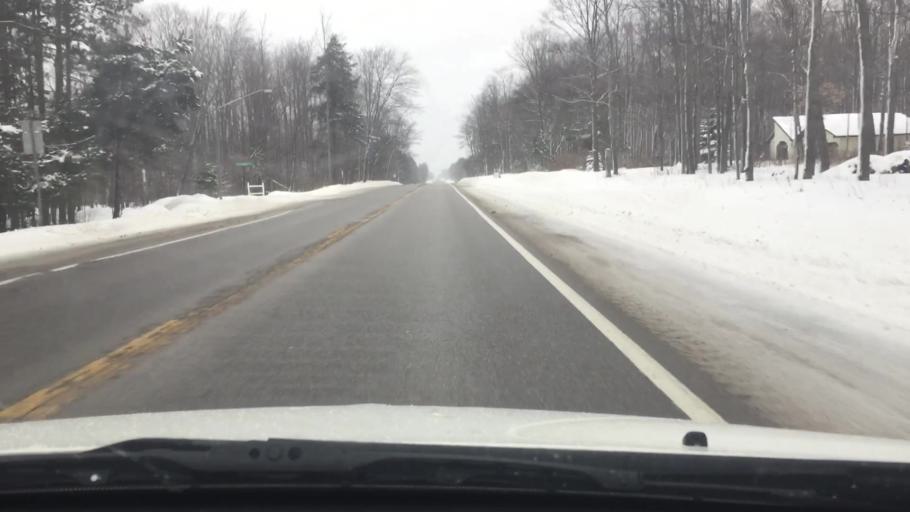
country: US
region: Michigan
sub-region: Otsego County
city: Gaylord
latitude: 45.0349
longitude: -84.7758
